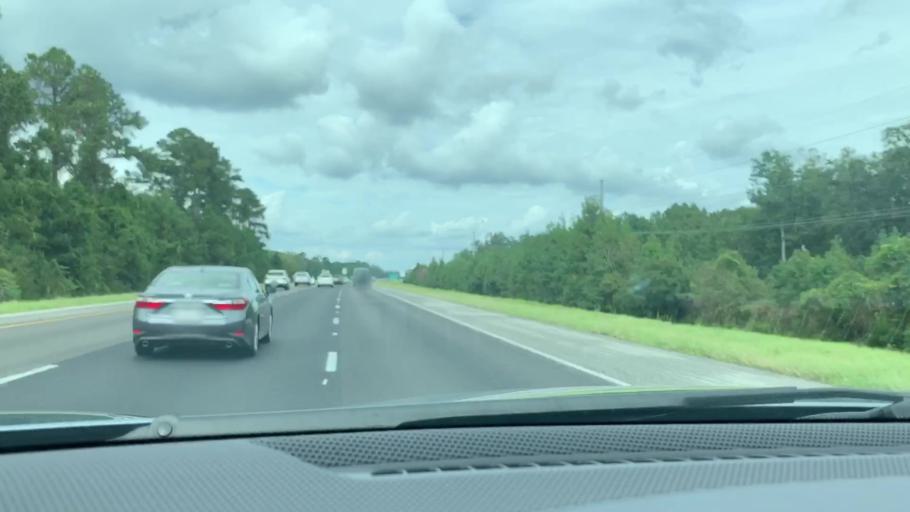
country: US
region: Georgia
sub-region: Liberty County
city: Midway
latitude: 31.7887
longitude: -81.3759
